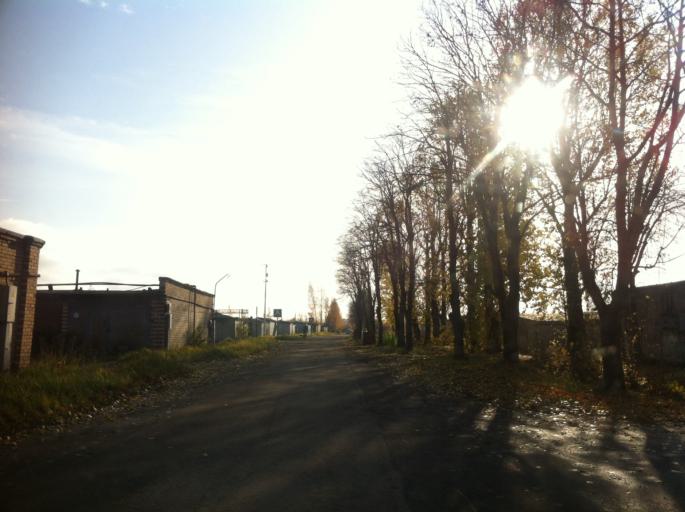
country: RU
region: St.-Petersburg
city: Uritsk
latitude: 59.8226
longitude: 30.1648
